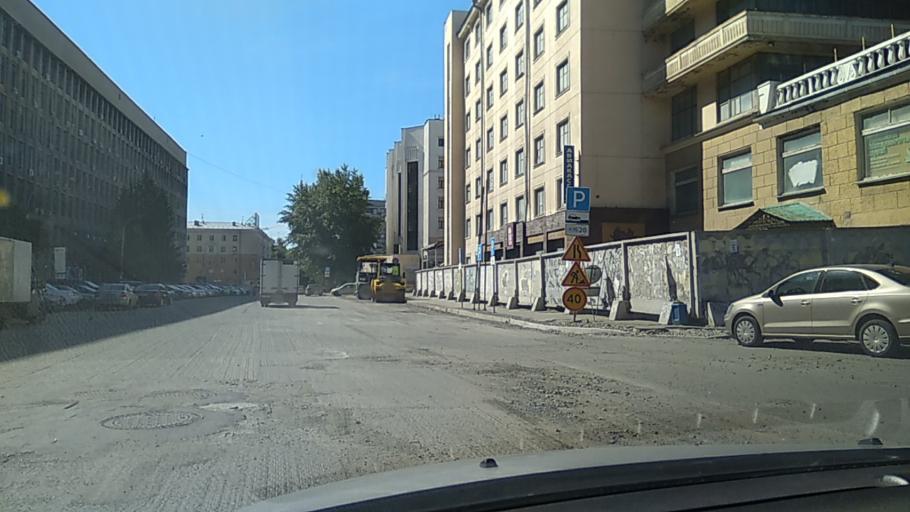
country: RU
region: Sverdlovsk
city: Yekaterinburg
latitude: 56.8378
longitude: 60.6186
